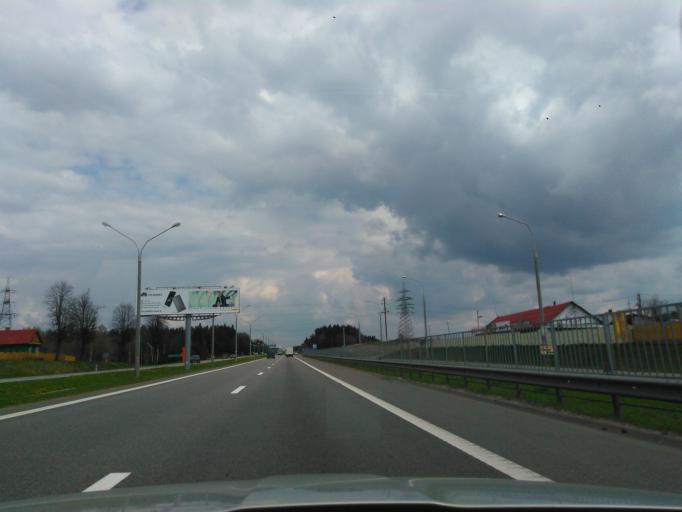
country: BY
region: Minsk
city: Korolev Stan
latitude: 53.9902
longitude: 27.8032
